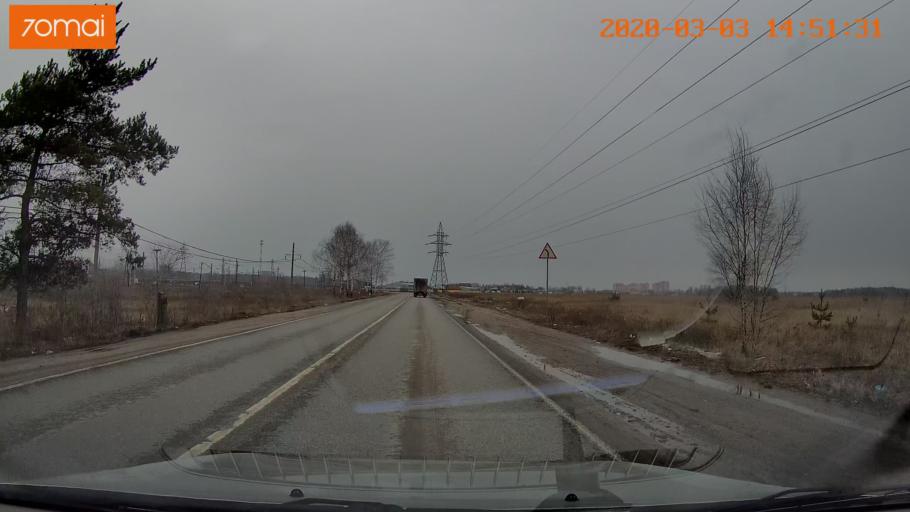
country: RU
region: Moskovskaya
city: Malakhovka
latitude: 55.6662
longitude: 38.0275
